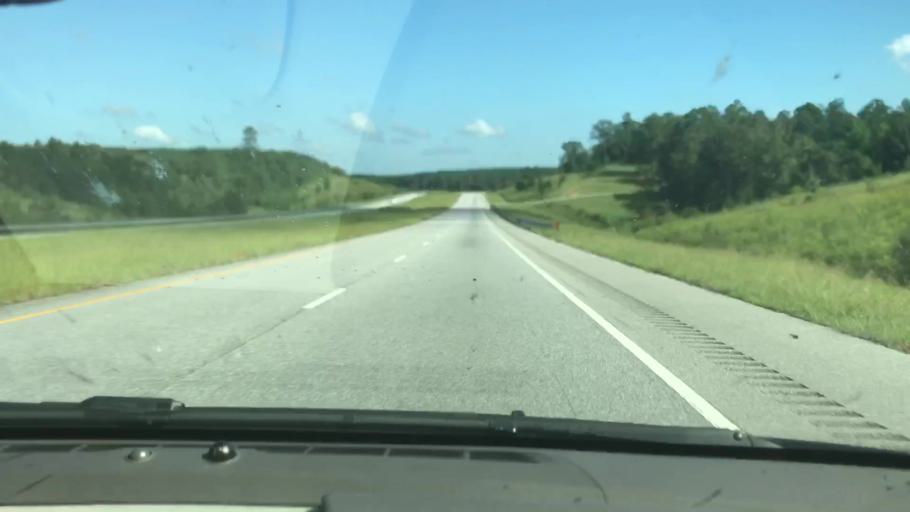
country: US
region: Alabama
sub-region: Barbour County
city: Eufaula
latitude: 32.1082
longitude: -85.1501
